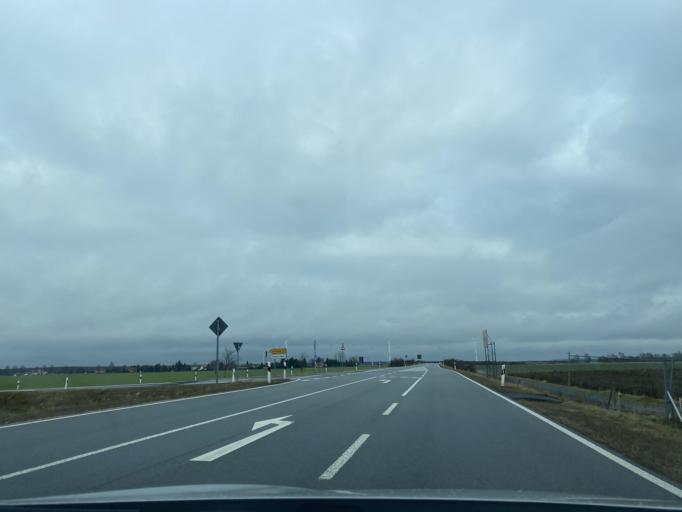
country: PL
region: Lower Silesian Voivodeship
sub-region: Powiat zgorzelecki
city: Piensk
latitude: 51.2350
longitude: 14.9805
